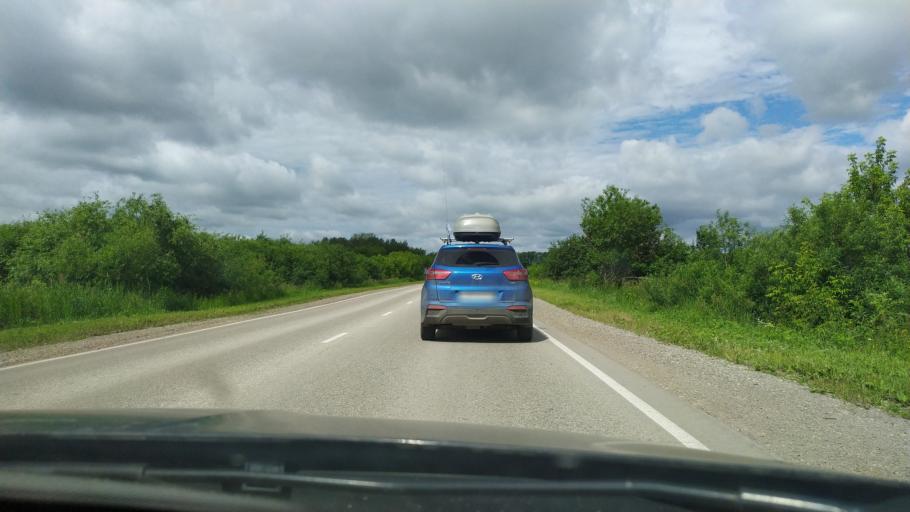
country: RU
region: Perm
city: Kondratovo
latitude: 57.9304
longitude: 56.0972
